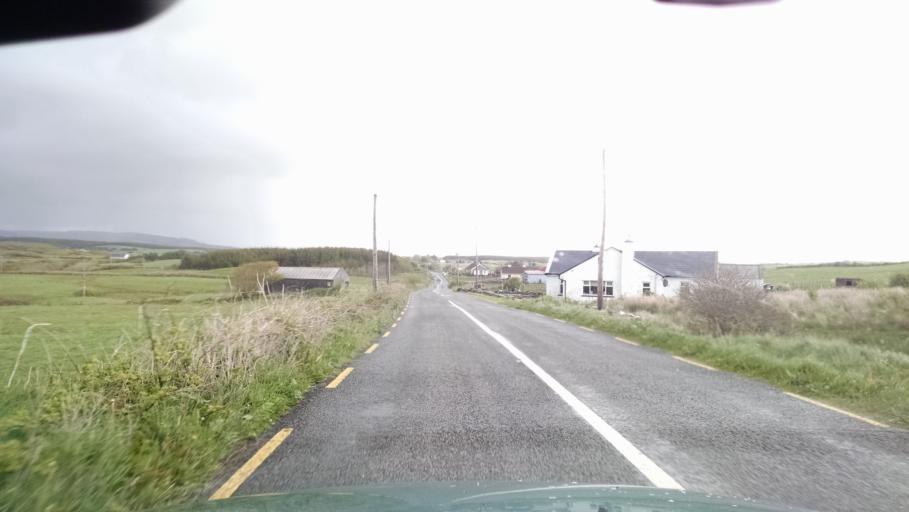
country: IE
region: Connaught
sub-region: County Galway
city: Bearna
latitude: 53.0159
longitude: -9.3232
